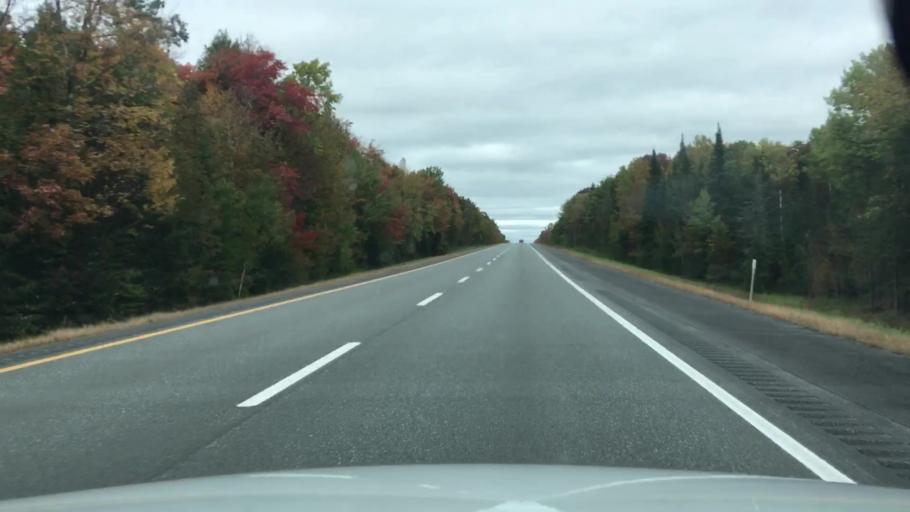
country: US
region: Maine
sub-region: Waldo County
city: Burnham
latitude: 44.7229
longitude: -69.4407
